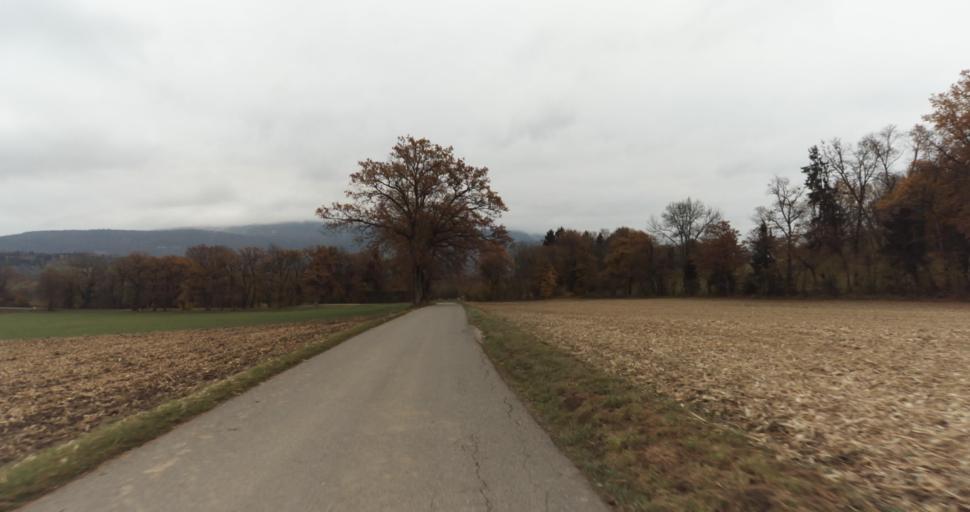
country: FR
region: Rhone-Alpes
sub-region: Departement de la Haute-Savoie
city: Chavanod
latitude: 45.8517
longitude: 6.0478
